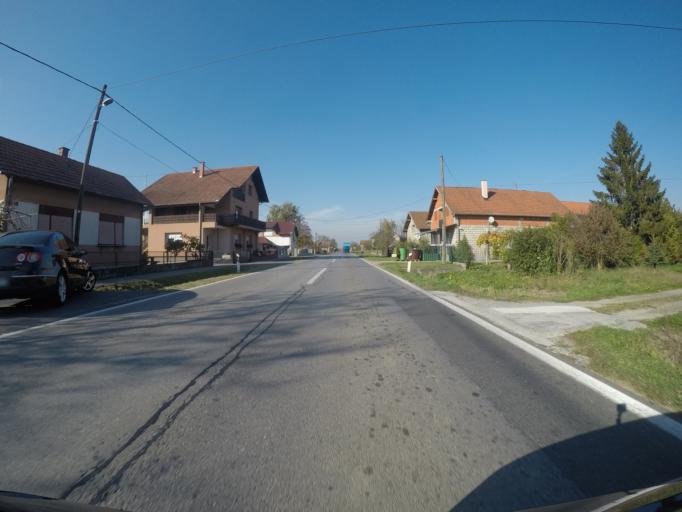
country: HR
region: Bjelovarsko-Bilogorska
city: Predavac
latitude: 45.9283
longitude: 16.7864
